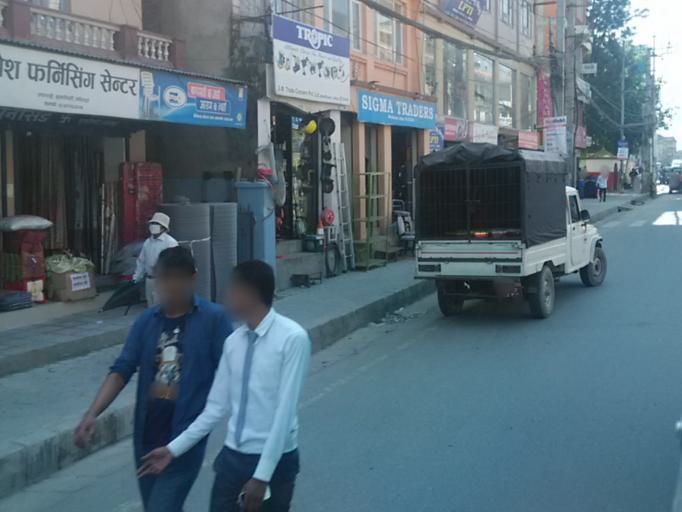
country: NP
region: Central Region
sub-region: Bagmati Zone
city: Patan
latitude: 27.6716
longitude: 85.3179
